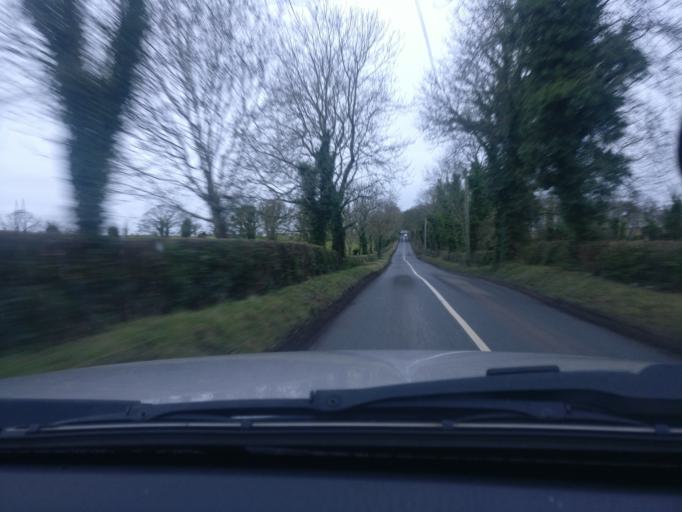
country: IE
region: Leinster
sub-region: An Mhi
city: Dunshaughlin
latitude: 53.4789
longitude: -6.6175
